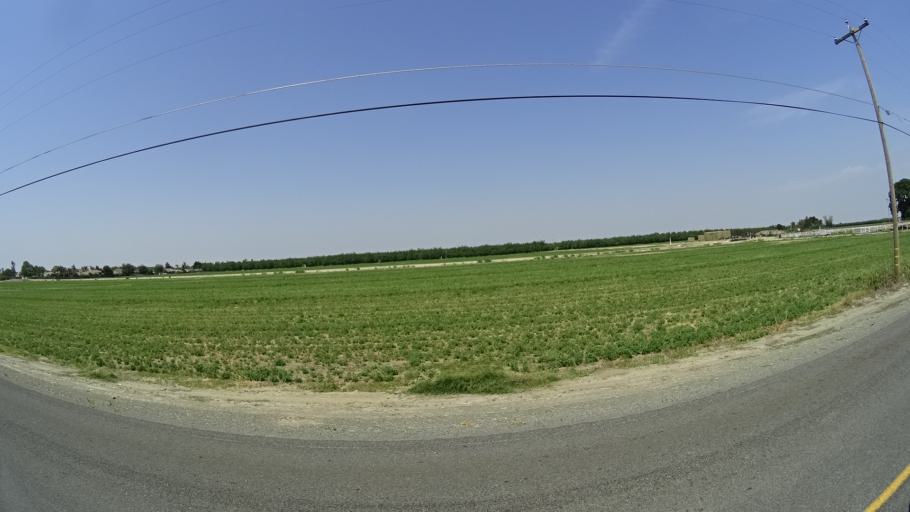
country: US
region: California
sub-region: Kings County
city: Lemoore
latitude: 36.3231
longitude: -119.7627
